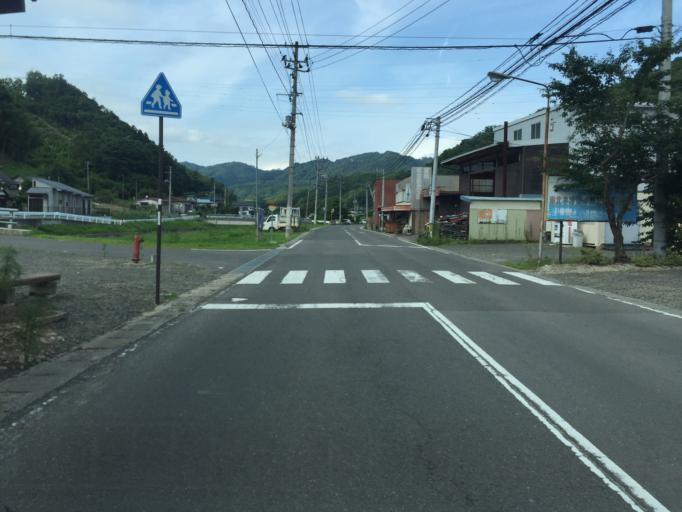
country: JP
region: Fukushima
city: Hobaramachi
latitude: 37.6712
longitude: 140.6110
